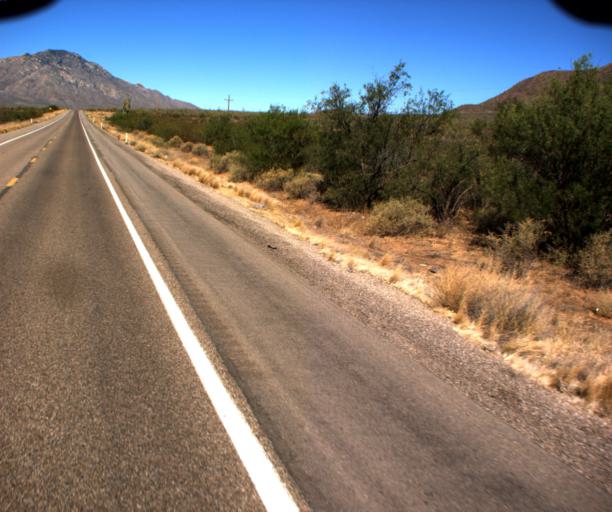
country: US
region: Arizona
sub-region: Pima County
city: Three Points
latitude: 32.0486
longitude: -111.4250
